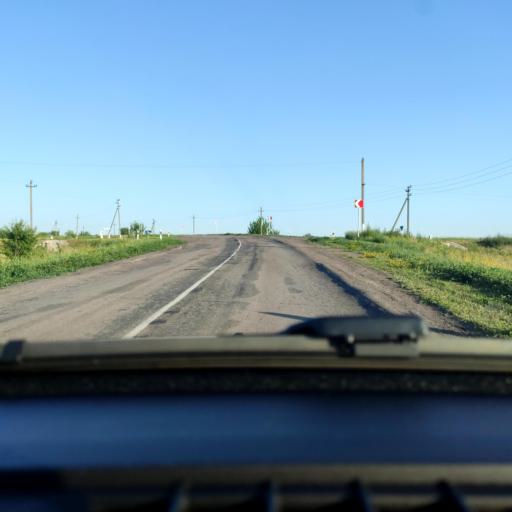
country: RU
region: Voronezj
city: Kashirskoye
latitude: 51.4978
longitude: 39.8348
